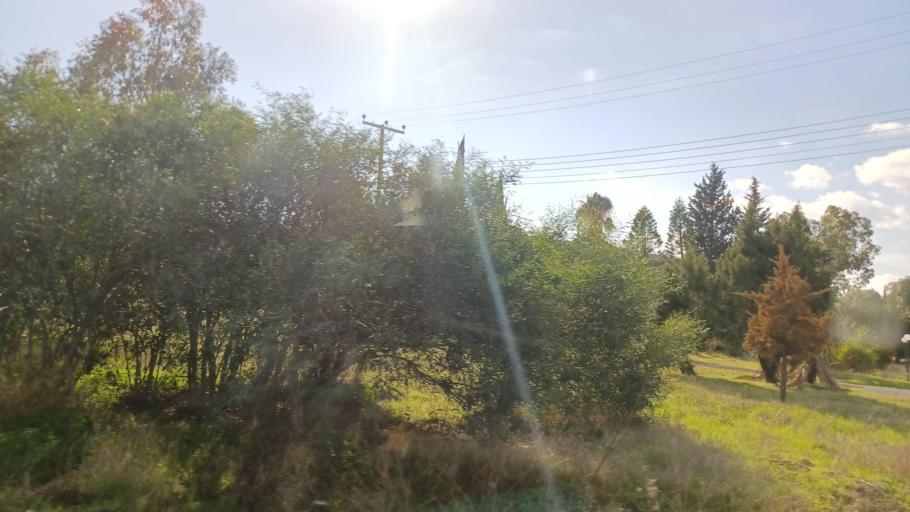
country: CY
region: Limassol
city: Pyrgos
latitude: 34.7346
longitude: 33.2156
